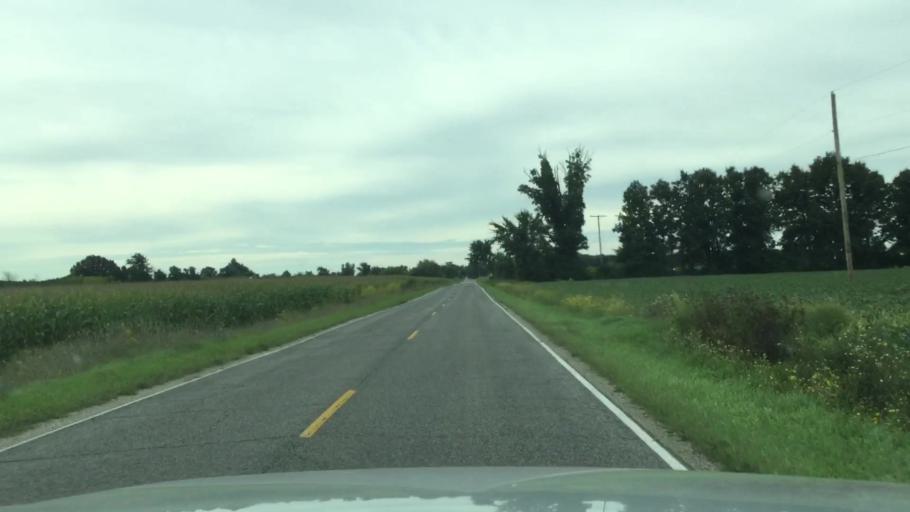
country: US
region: Michigan
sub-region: Genesee County
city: Flushing
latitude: 43.0672
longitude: -83.9876
